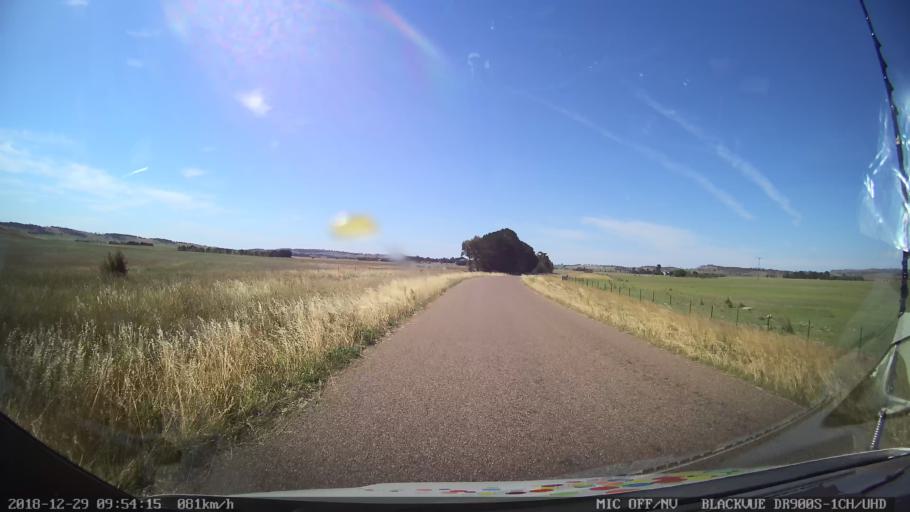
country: AU
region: New South Wales
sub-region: Goulburn Mulwaree
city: Goulburn
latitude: -34.7609
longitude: 149.4672
